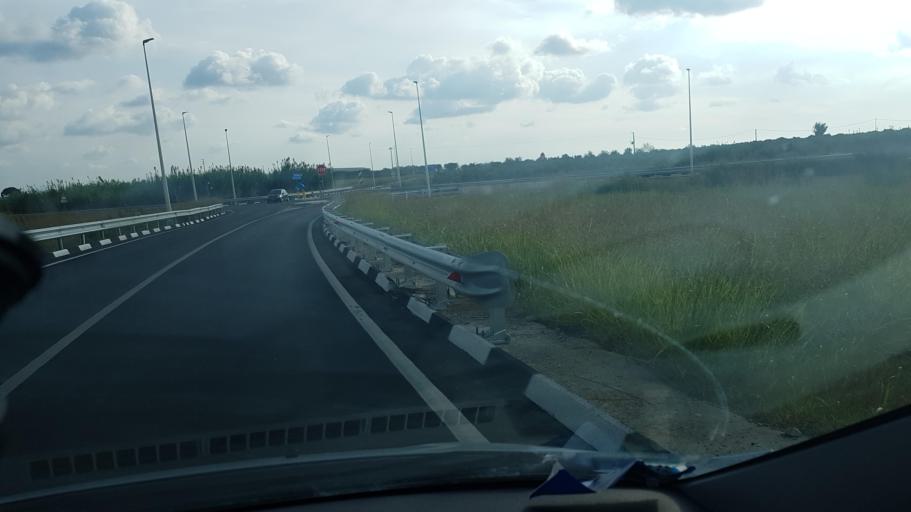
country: IT
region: Apulia
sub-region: Provincia di Brindisi
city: Cellino San Marco
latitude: 40.4397
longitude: 17.9552
